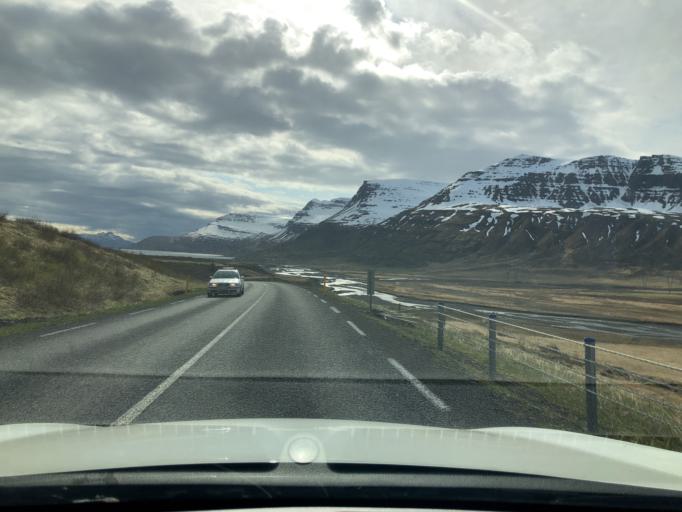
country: IS
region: East
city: Reydarfjoerdur
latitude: 65.0339
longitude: -14.3304
